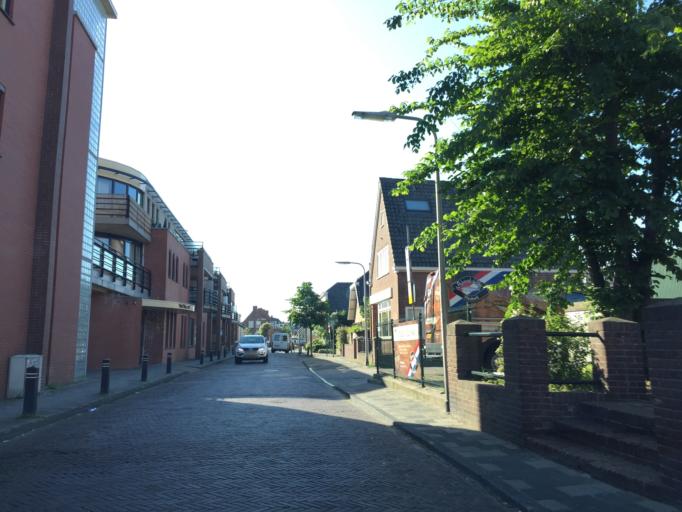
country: NL
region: South Holland
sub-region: Gemeente Noordwijk
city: Noordwijk-Binnen
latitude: 52.2432
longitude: 4.4365
